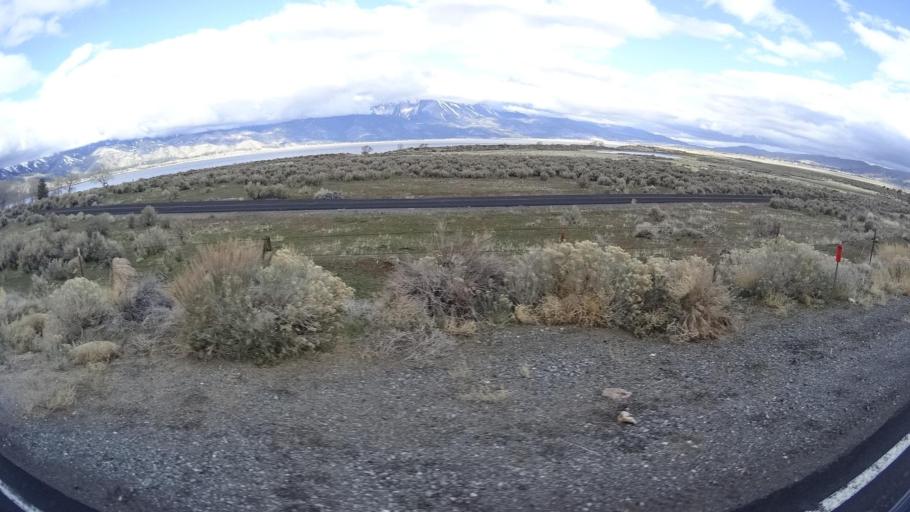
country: US
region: Nevada
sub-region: Carson City
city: Carson City
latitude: 39.2394
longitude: -119.7650
